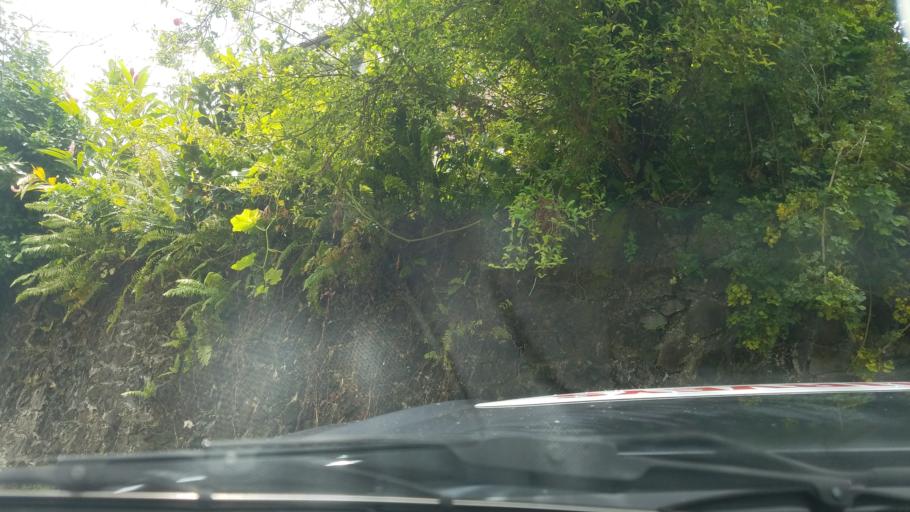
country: LC
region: Castries Quarter
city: Bisee
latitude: 14.0020
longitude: -60.9755
